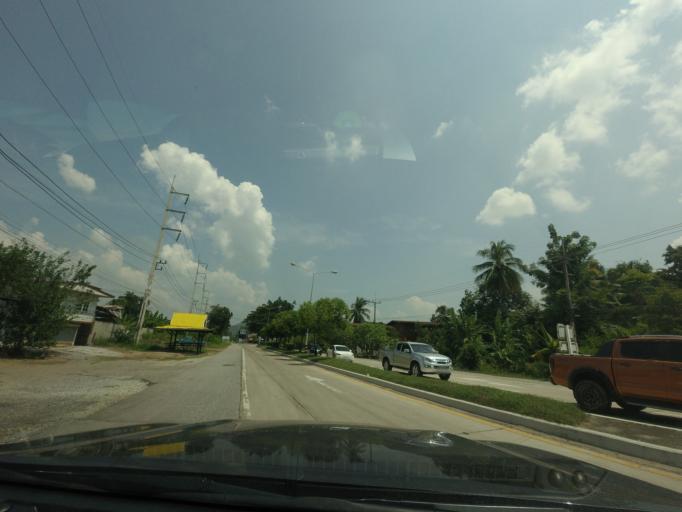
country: TH
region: Uttaradit
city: Thong Saen Khan
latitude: 17.4715
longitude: 100.2366
